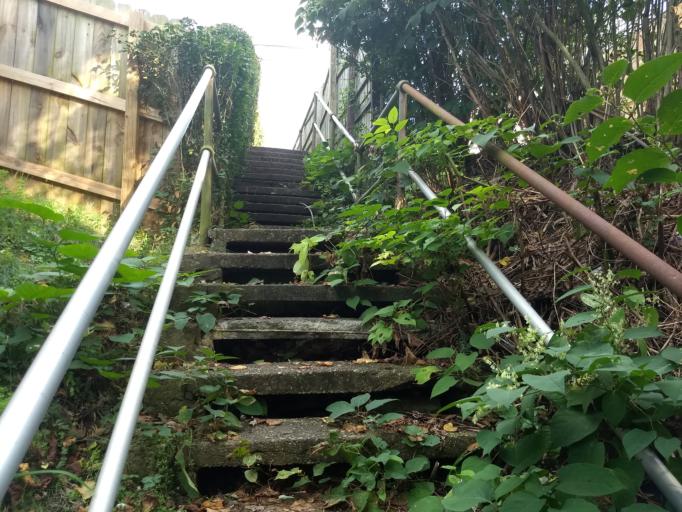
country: US
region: Pennsylvania
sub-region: Allegheny County
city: Dormont
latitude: 40.4027
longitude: -80.0323
